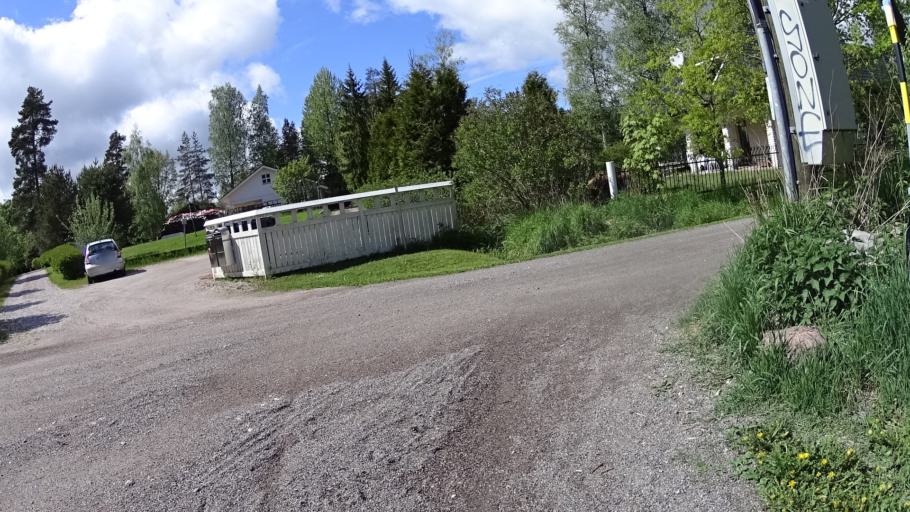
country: FI
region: Uusimaa
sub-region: Helsinki
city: Kilo
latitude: 60.2338
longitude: 24.7582
